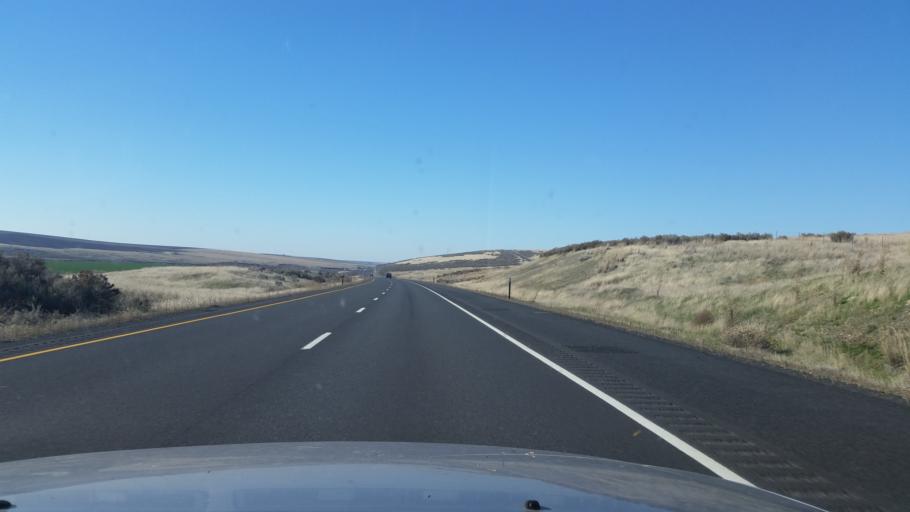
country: US
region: Washington
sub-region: Grant County
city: Warden
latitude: 47.0849
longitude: -118.9637
